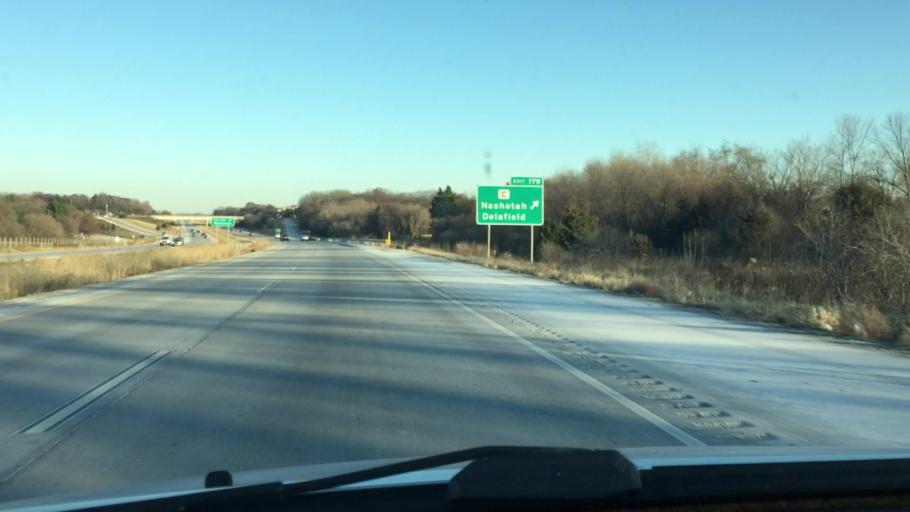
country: US
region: Wisconsin
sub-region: Waukesha County
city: Nashotah
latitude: 43.1017
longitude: -88.4129
